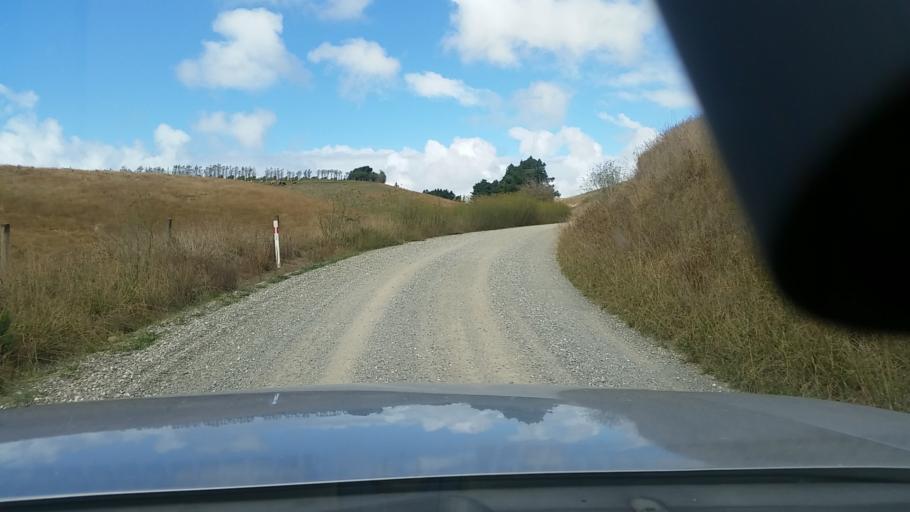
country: NZ
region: Marlborough
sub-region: Marlborough District
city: Blenheim
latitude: -41.6891
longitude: 174.1402
